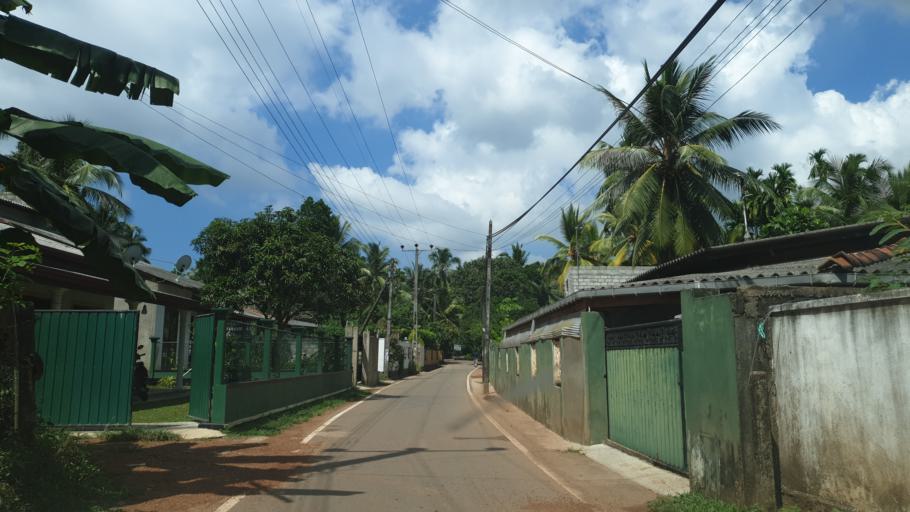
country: LK
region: Western
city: Panadura
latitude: 6.6763
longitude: 79.9715
